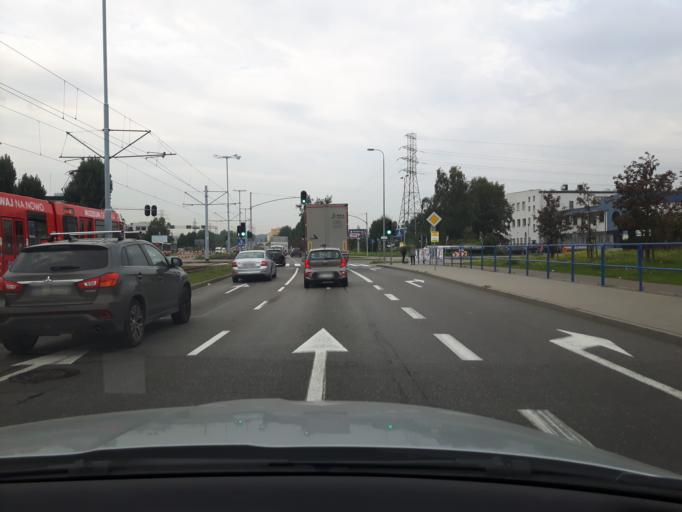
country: PL
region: Pomeranian Voivodeship
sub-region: Gdansk
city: Gdansk
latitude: 54.3843
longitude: 18.6412
